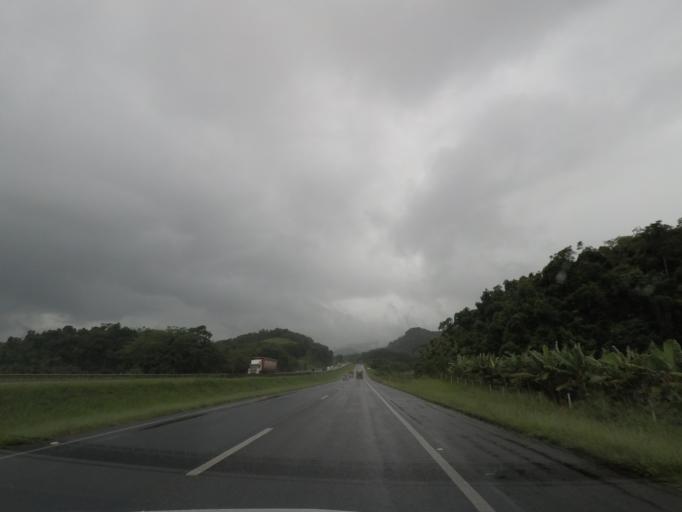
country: BR
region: Sao Paulo
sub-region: Juquia
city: Juquia
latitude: -24.3333
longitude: -47.6023
